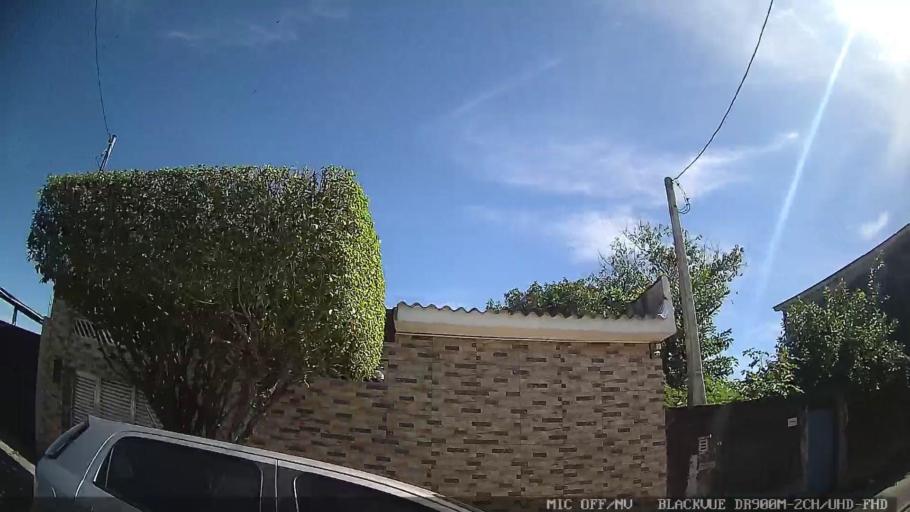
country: BR
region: Sao Paulo
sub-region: Santos
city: Santos
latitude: -23.9420
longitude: -46.2826
